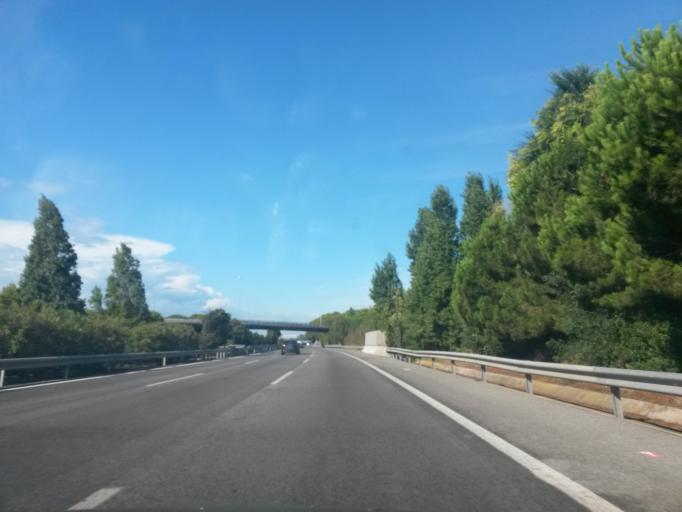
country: ES
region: Catalonia
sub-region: Provincia de Barcelona
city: Sant Andreu de Llavaneres
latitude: 41.5623
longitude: 2.4899
